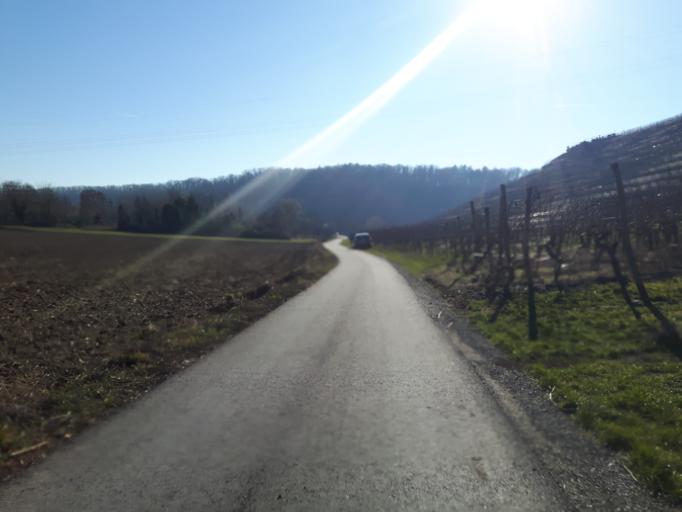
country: DE
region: Baden-Wuerttemberg
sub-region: Regierungsbezirk Stuttgart
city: Lauffen am Neckar
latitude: 49.0698
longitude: 9.1288
